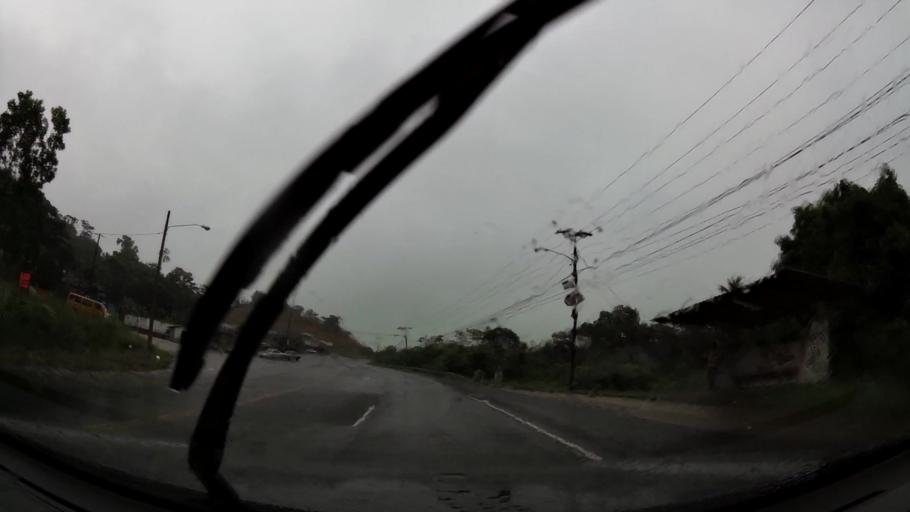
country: PA
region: Colon
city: Rio Rita
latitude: 9.3057
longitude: -79.7845
